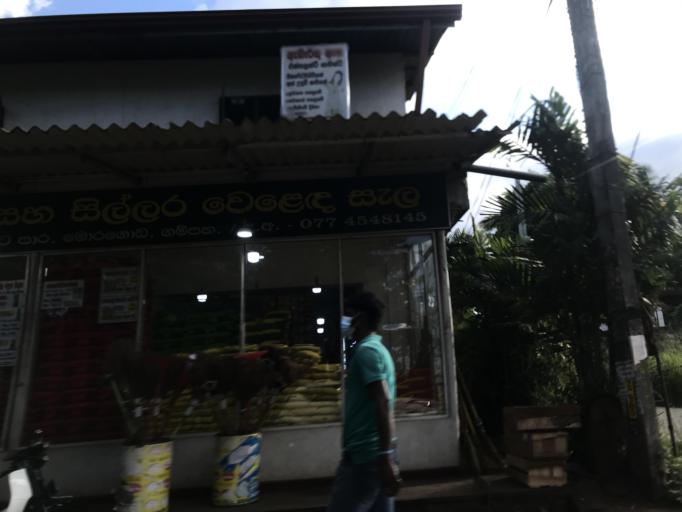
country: LK
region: Western
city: Gampaha
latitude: 7.0733
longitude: 79.9985
